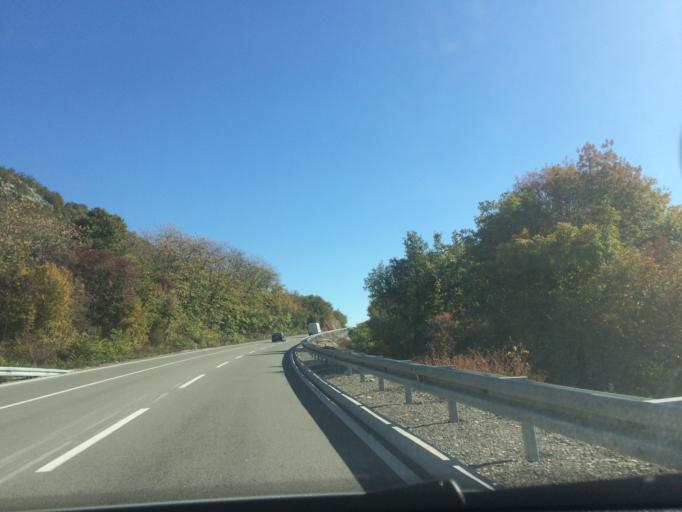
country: ME
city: Mojanovici
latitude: 42.3872
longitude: 19.0729
